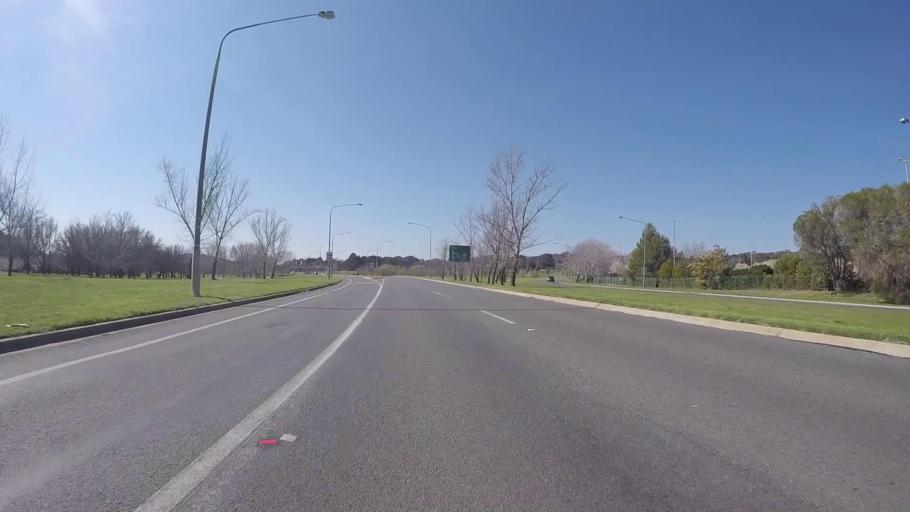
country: AU
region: Australian Capital Territory
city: Forrest
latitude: -35.3376
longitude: 149.0845
